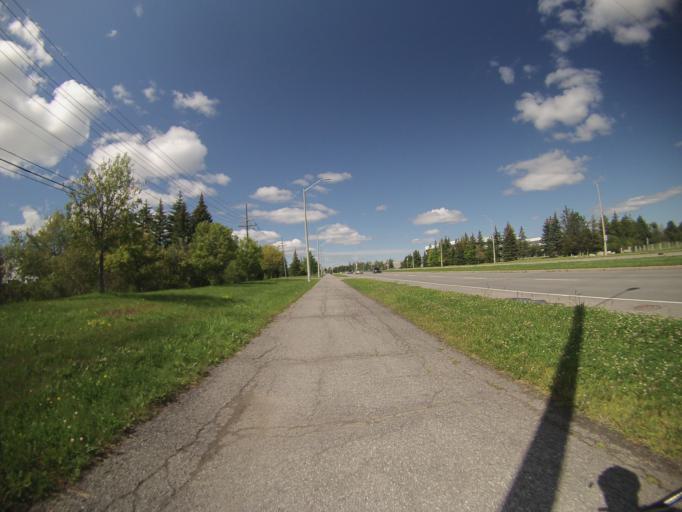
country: CA
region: Ontario
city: Ottawa
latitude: 45.3791
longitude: -75.6276
